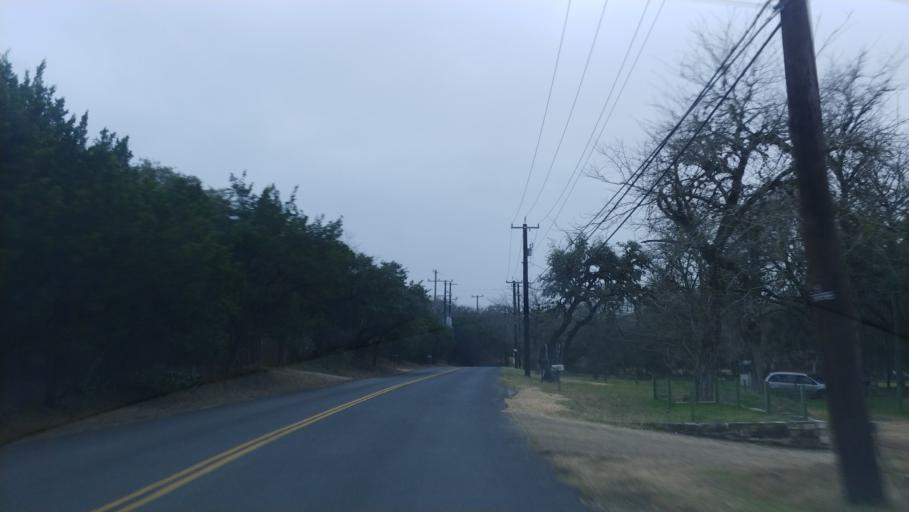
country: US
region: Texas
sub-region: Bexar County
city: Cross Mountain
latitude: 29.6283
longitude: -98.6826
